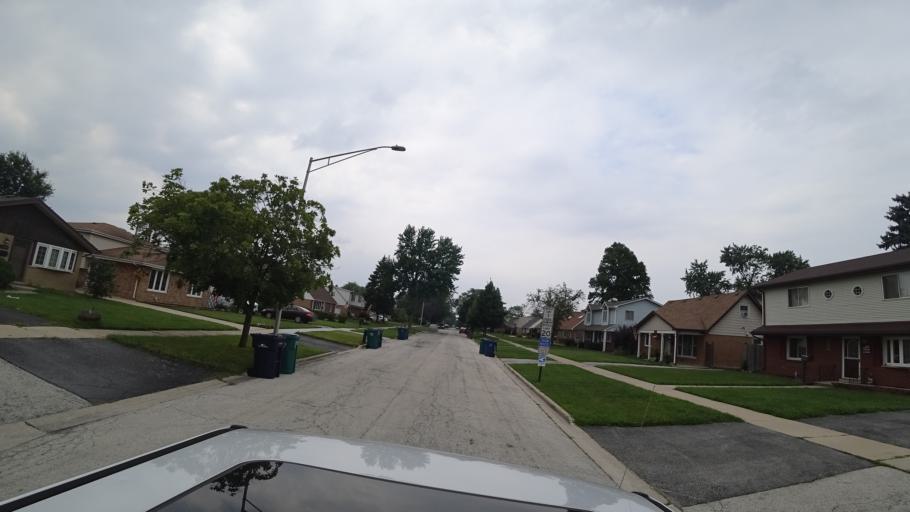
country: US
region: Illinois
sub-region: Cook County
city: Chicago Ridge
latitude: 41.6910
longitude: -87.7629
